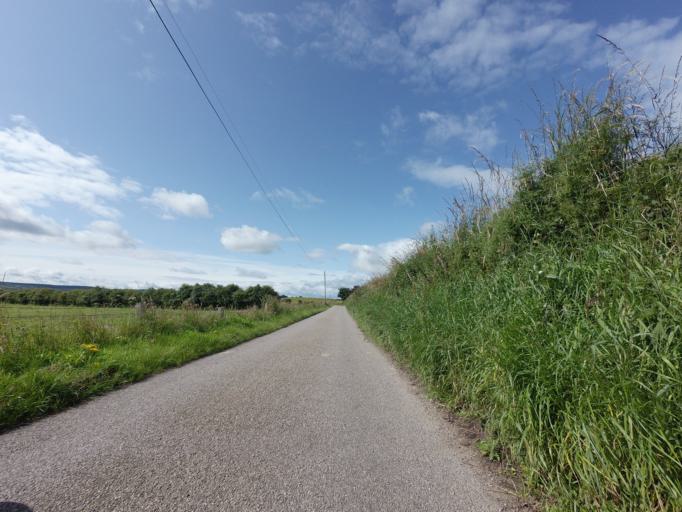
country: GB
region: Scotland
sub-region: Moray
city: Burghead
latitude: 57.6504
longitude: -3.5032
